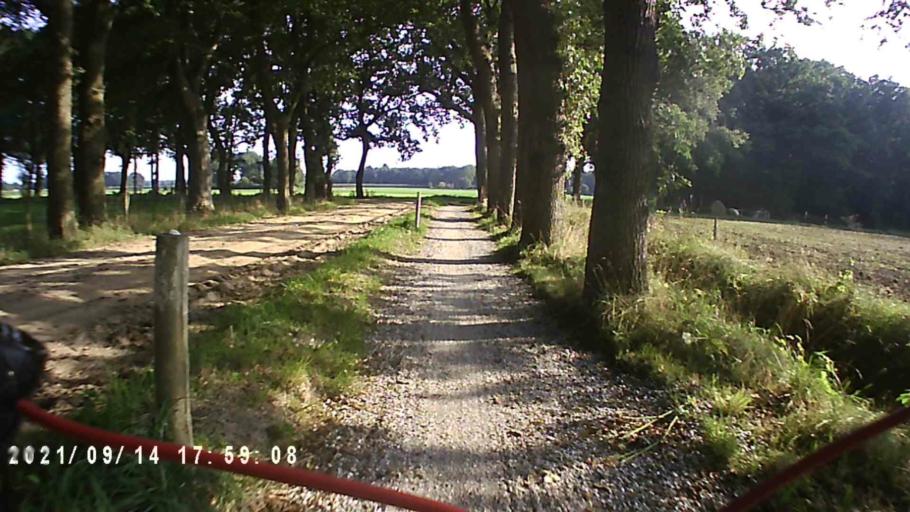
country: NL
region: Drenthe
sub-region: Gemeente Tynaarlo
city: Zuidlaren
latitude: 53.1240
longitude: 6.6498
